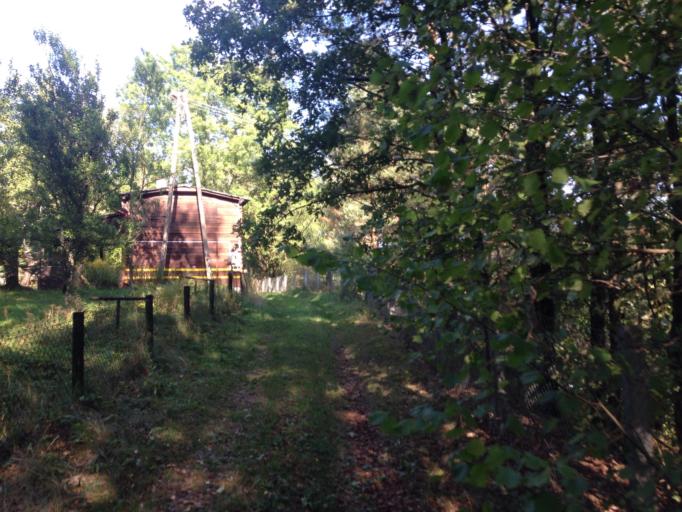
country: PL
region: Kujawsko-Pomorskie
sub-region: Powiat brodnicki
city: Gorzno
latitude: 53.2331
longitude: 19.7046
